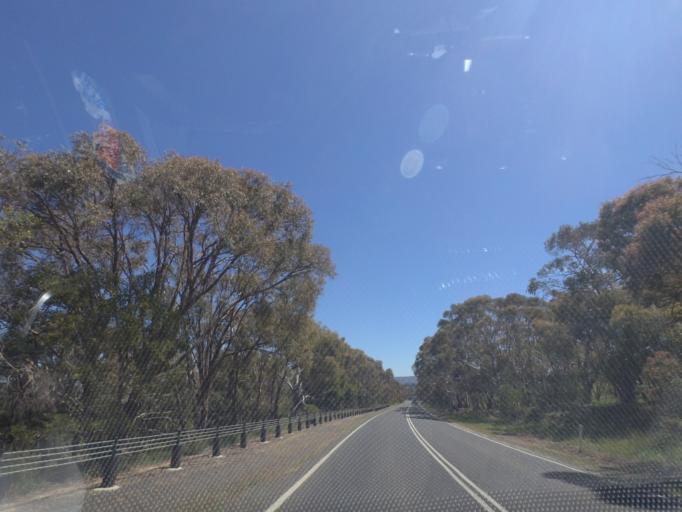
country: AU
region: Victoria
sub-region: Hume
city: Sunbury
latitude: -37.2901
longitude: 144.7897
